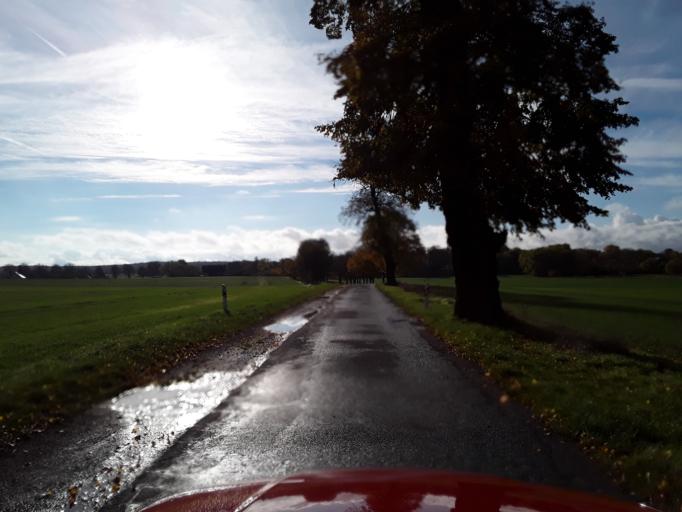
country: DE
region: Brandenburg
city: Mittenwalde
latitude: 53.2759
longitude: 13.7007
